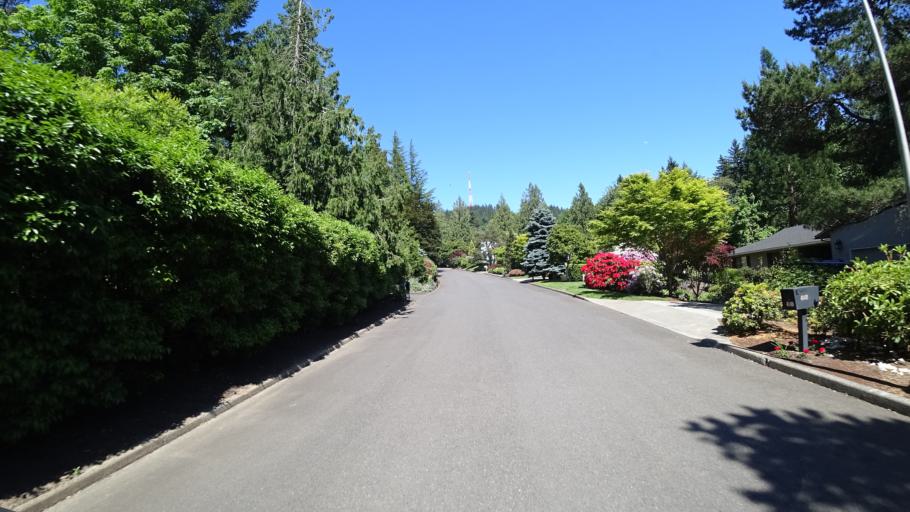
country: US
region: Oregon
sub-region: Washington County
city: West Slope
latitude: 45.4965
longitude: -122.7196
